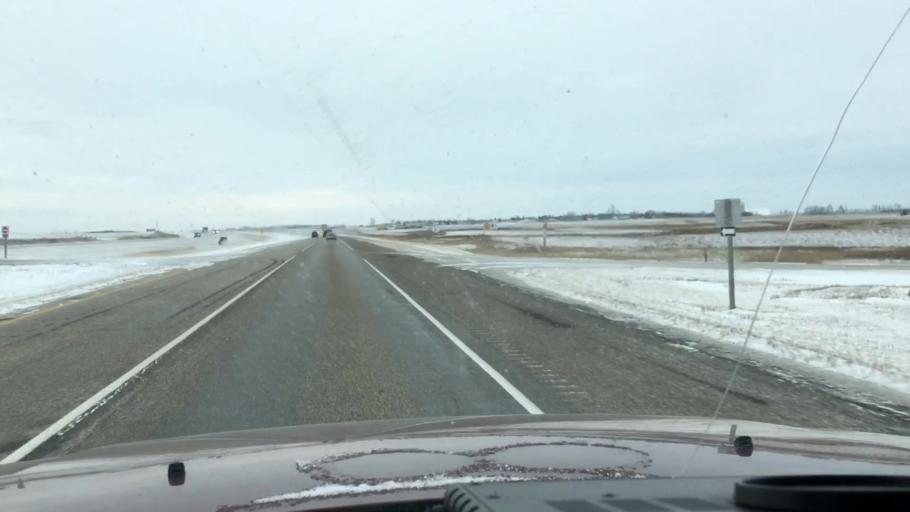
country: CA
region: Saskatchewan
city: Saskatoon
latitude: 51.6492
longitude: -106.4396
